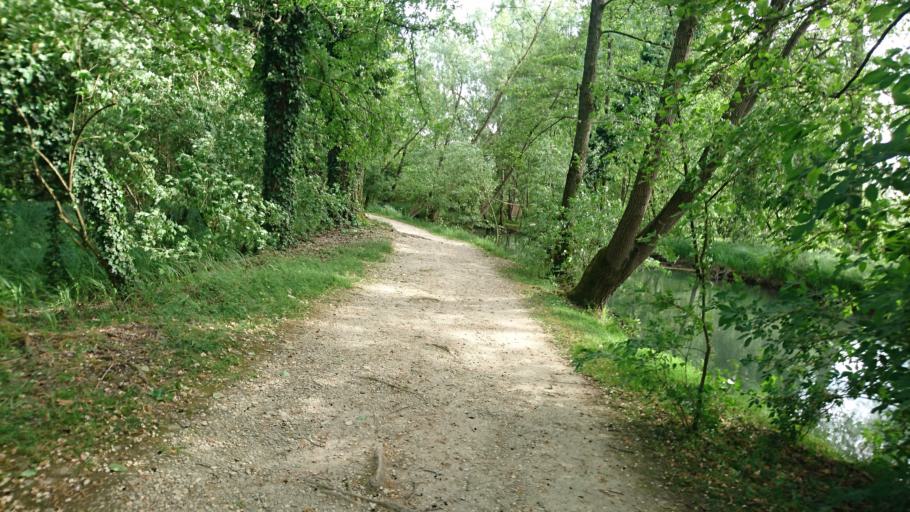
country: IT
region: Veneto
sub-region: Provincia di Treviso
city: Santa Cristina
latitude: 45.6436
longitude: 12.1272
